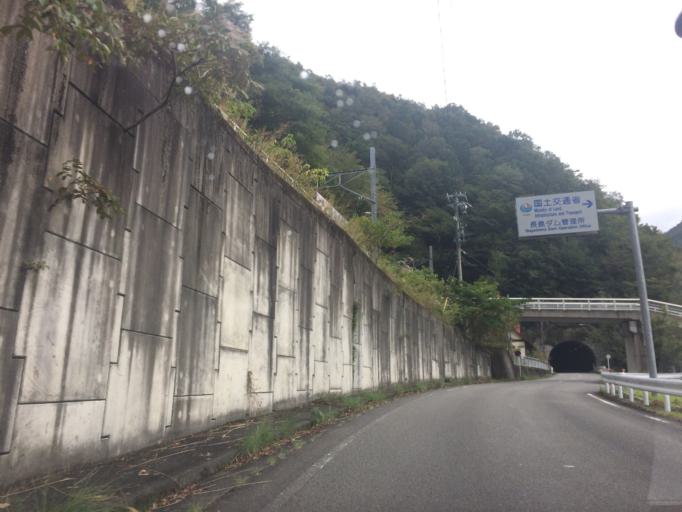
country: JP
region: Shizuoka
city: Shizuoka-shi
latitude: 35.1694
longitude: 138.1564
